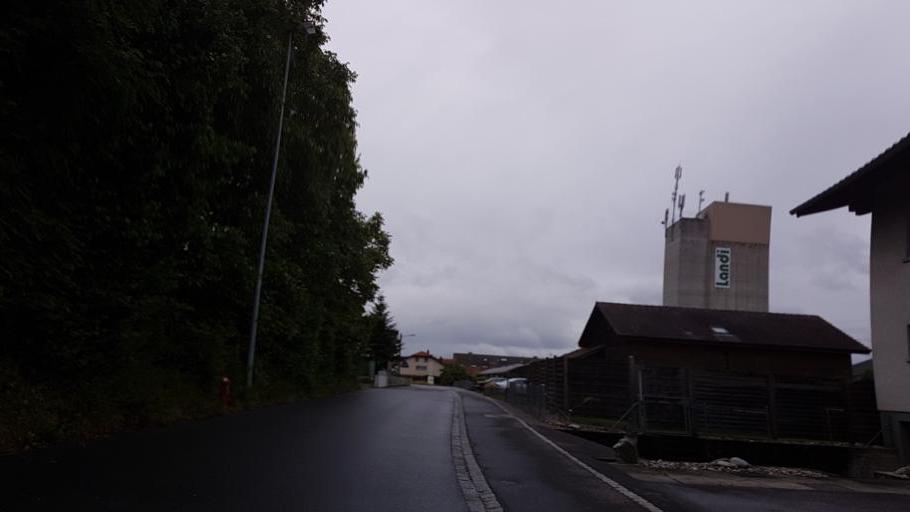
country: CH
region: Bern
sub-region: Bern-Mittelland District
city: Niederwichtrach
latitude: 46.8462
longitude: 7.5687
